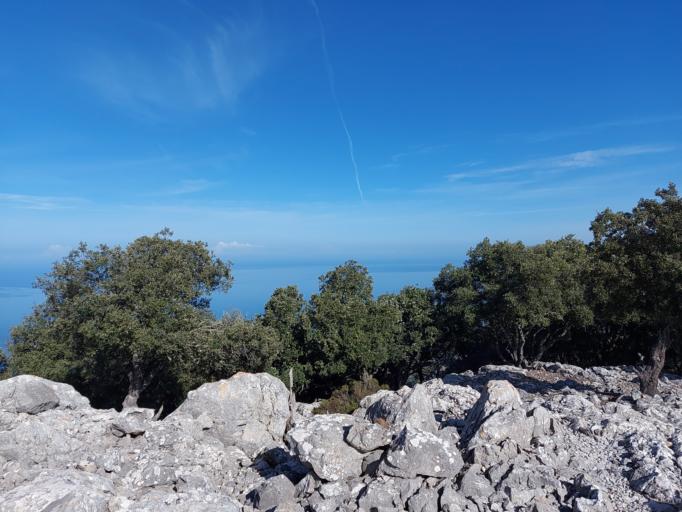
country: ES
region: Balearic Islands
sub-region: Illes Balears
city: Valldemossa
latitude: 39.7281
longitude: 2.6152
